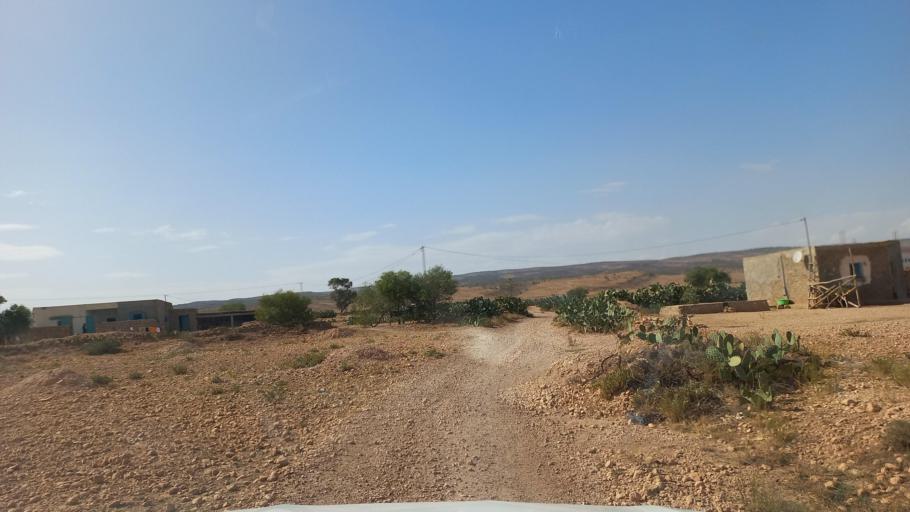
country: TN
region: Al Qasrayn
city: Kasserine
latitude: 35.2862
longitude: 8.9386
